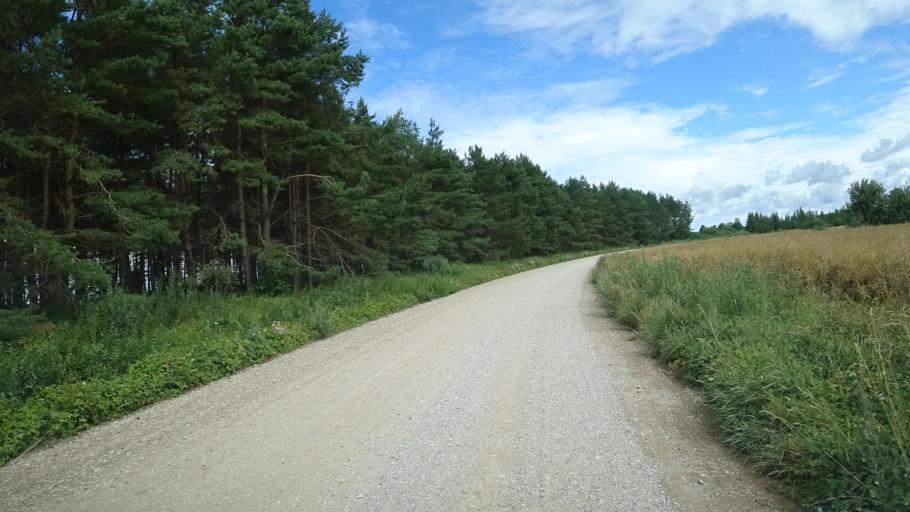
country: LV
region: Liepaja
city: Vec-Liepaja
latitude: 56.6468
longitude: 21.0446
